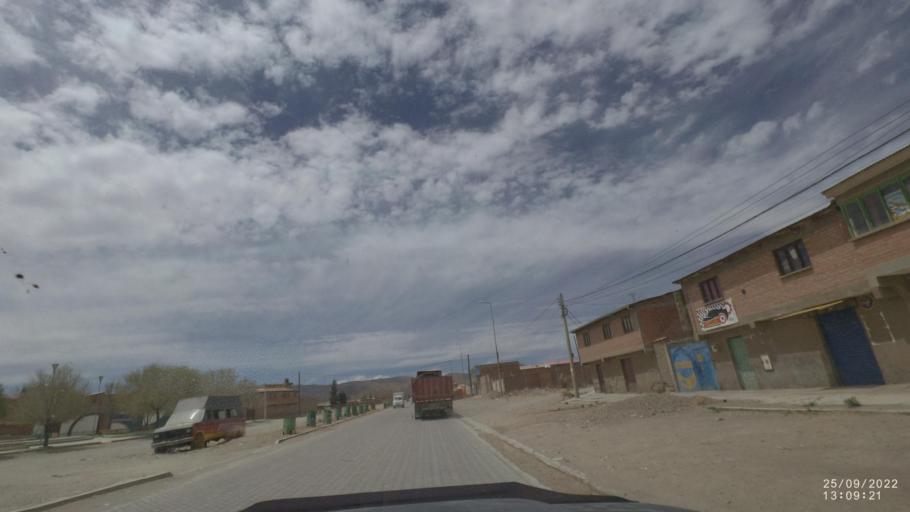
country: BO
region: Oruro
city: Oruro
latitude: -17.9755
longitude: -67.0570
